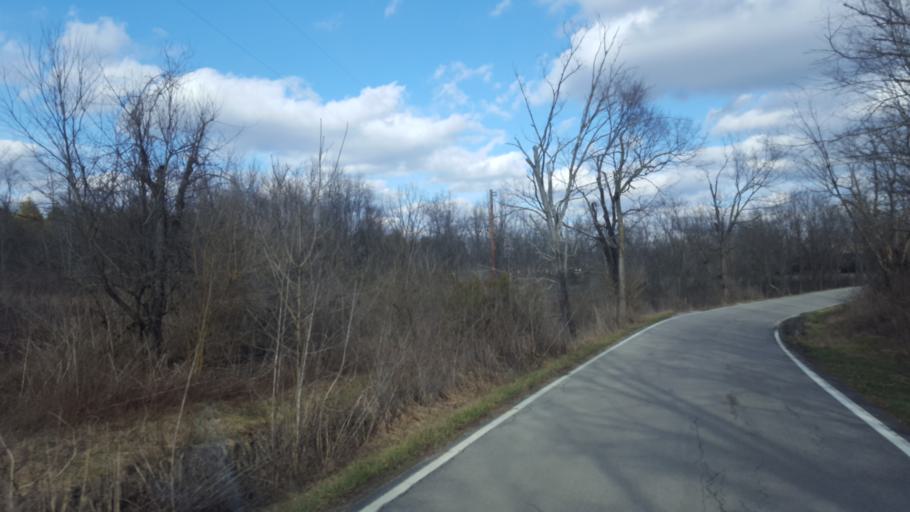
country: US
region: Kentucky
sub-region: Scott County
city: Georgetown
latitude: 38.3036
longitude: -84.5386
